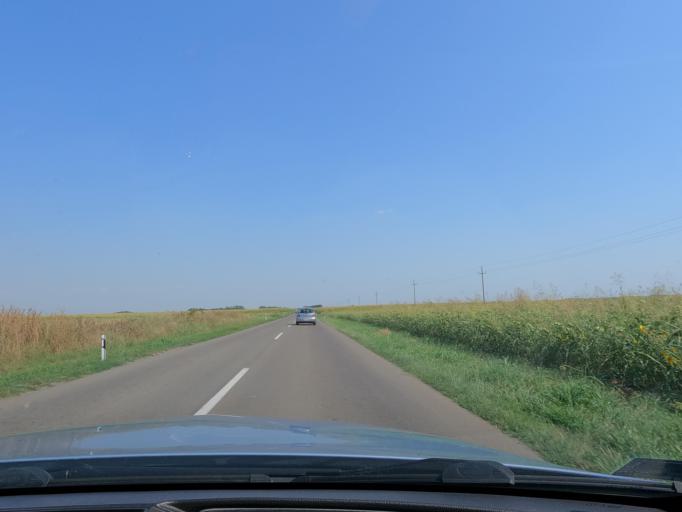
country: RS
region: Autonomna Pokrajina Vojvodina
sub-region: Severnobacki Okrug
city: Backa Topola
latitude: 45.7981
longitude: 19.6657
